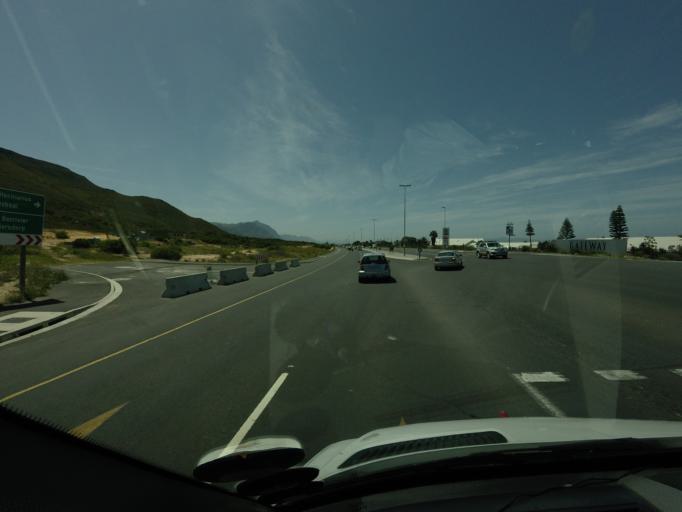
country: ZA
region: Western Cape
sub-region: Overberg District Municipality
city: Hermanus
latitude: -34.4182
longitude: 19.2192
